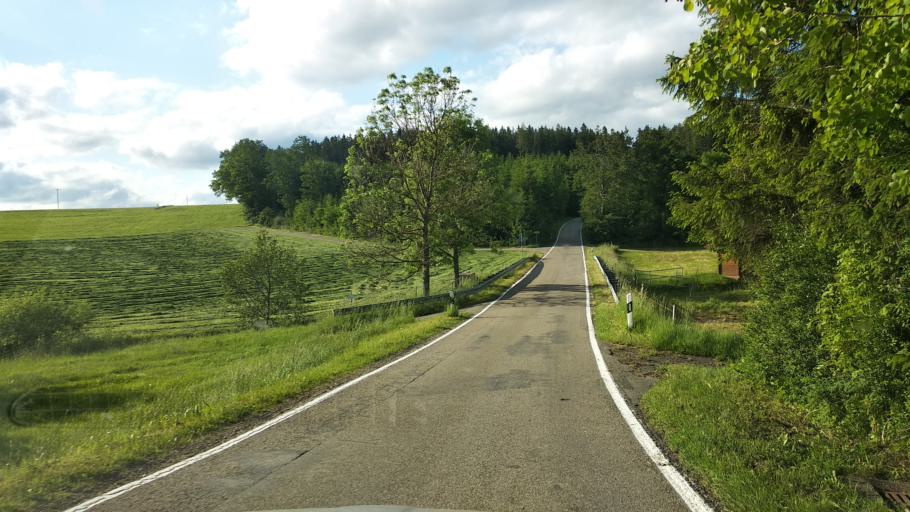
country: DE
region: Baden-Wuerttemberg
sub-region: Tuebingen Region
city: Aitrach
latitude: 47.9513
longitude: 10.0416
